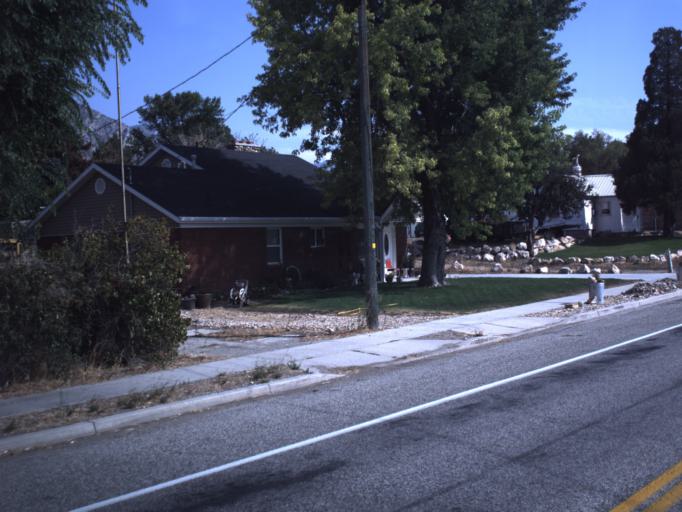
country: US
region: Utah
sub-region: Box Elder County
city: Honeyville
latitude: 41.6384
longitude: -112.0796
